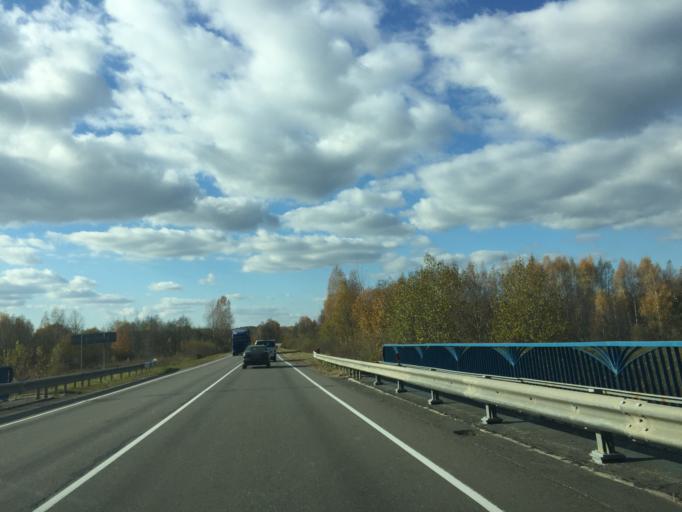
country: BY
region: Vitebsk
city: Pastavy
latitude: 55.0058
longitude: 26.8555
